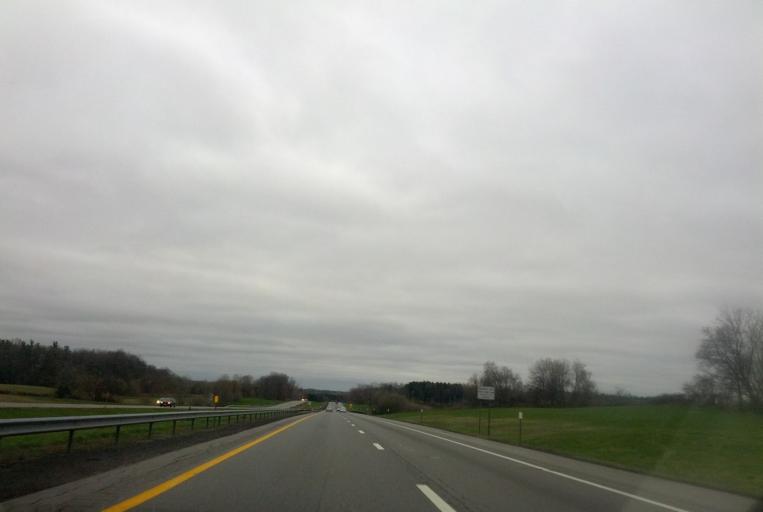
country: US
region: New York
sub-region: Ontario County
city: Phelps
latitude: 42.9554
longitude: -77.0081
